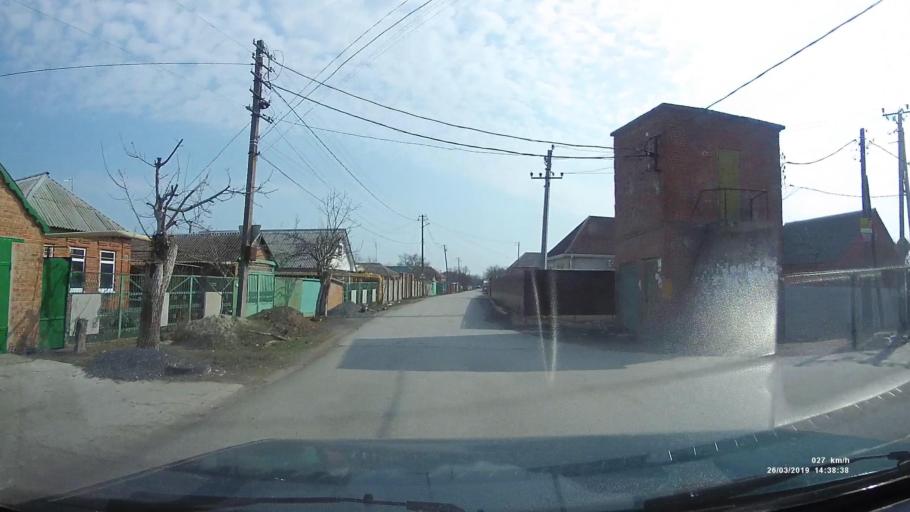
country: RU
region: Rostov
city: Novobessergenovka
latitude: 47.1816
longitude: 38.8619
